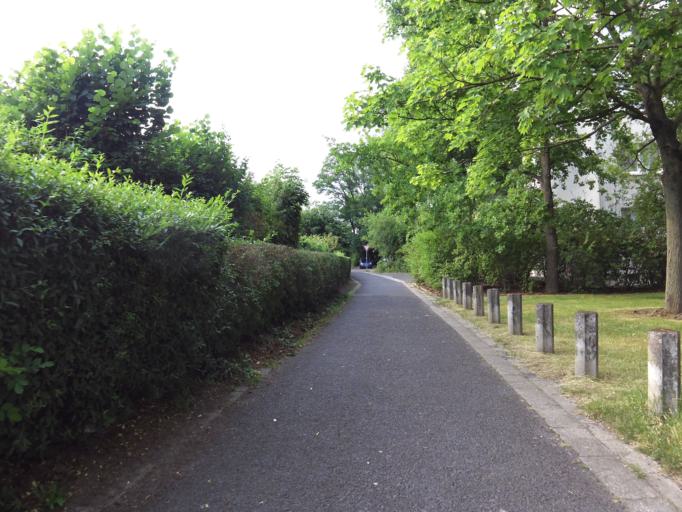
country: DE
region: Saxony
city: Markkleeberg
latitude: 51.3062
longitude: 12.3189
